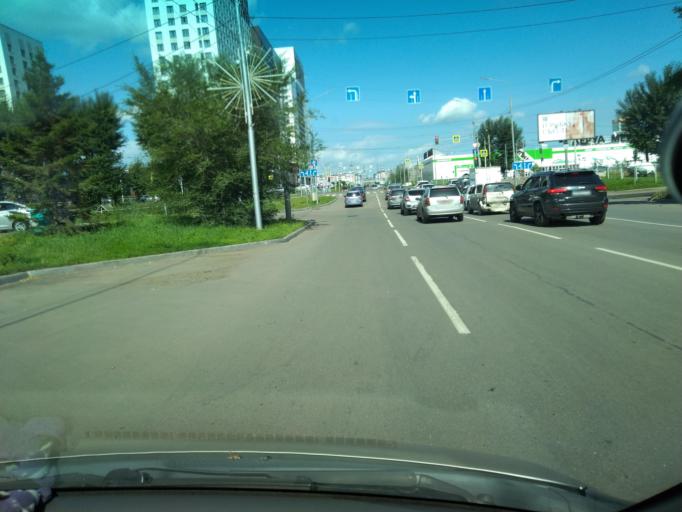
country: RU
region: Krasnoyarskiy
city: Krasnoyarsk
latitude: 56.0463
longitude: 92.9044
